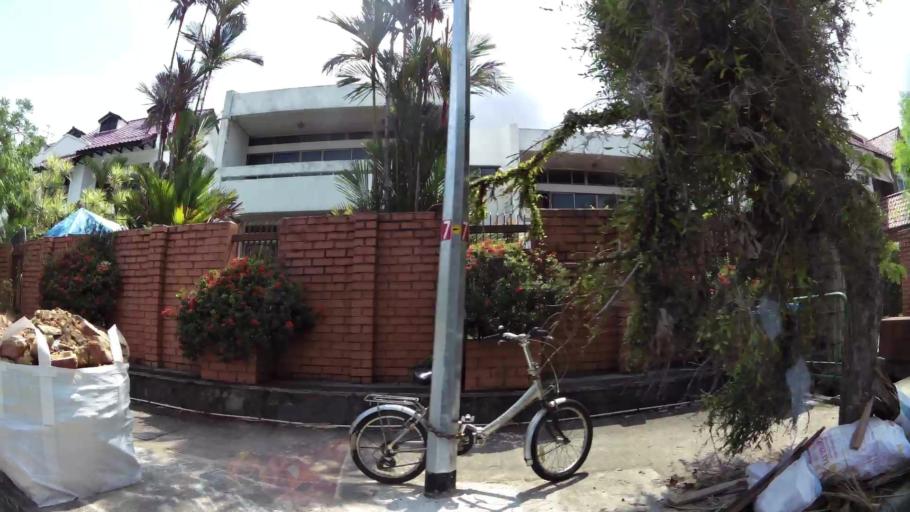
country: SG
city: Singapore
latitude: 1.3226
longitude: 103.8097
